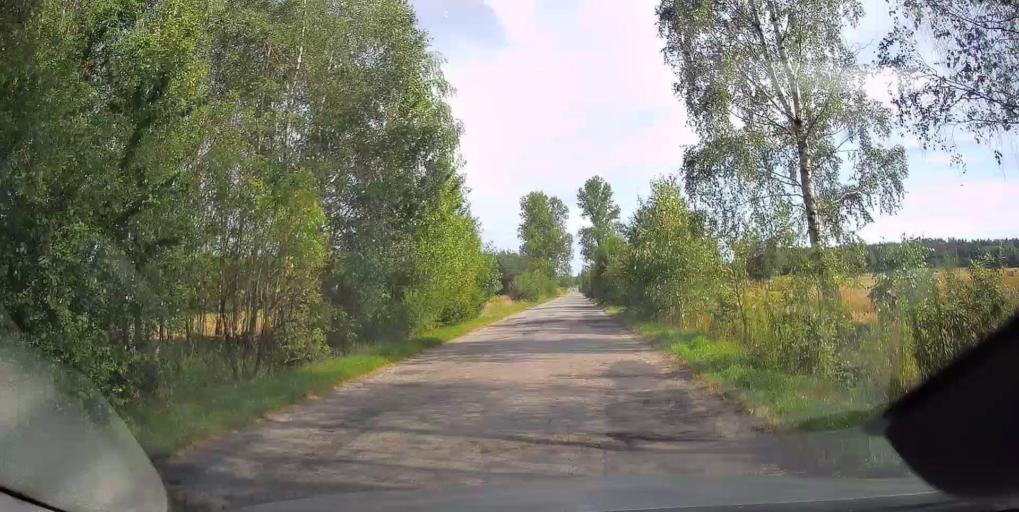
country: GB
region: England
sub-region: Greater London
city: Bromley
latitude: 51.4167
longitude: 0.0000
